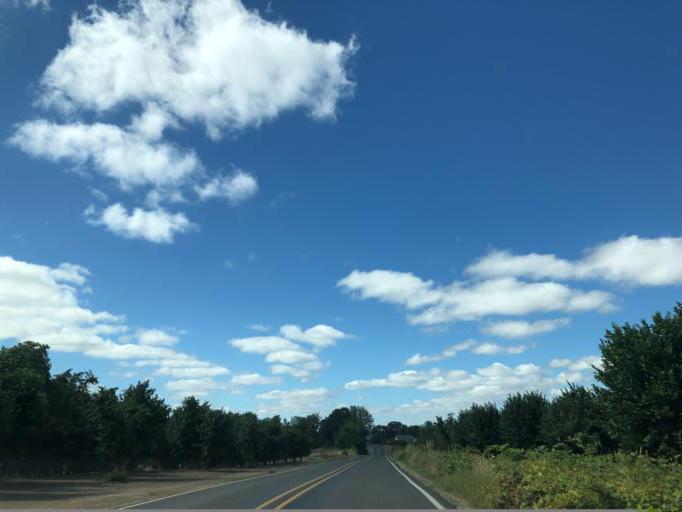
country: US
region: Oregon
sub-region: Marion County
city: Mount Angel
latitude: 45.1053
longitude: -122.7294
